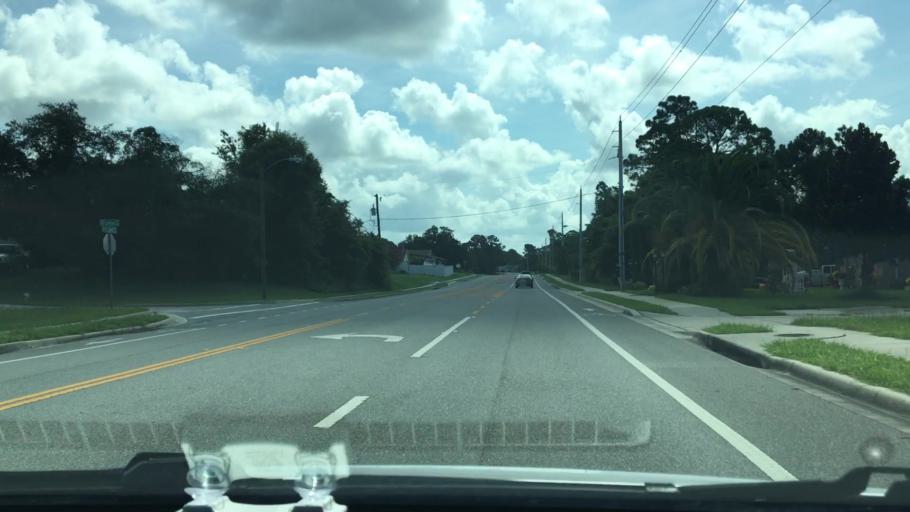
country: US
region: Florida
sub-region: Volusia County
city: Deltona
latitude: 28.8773
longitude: -81.1905
